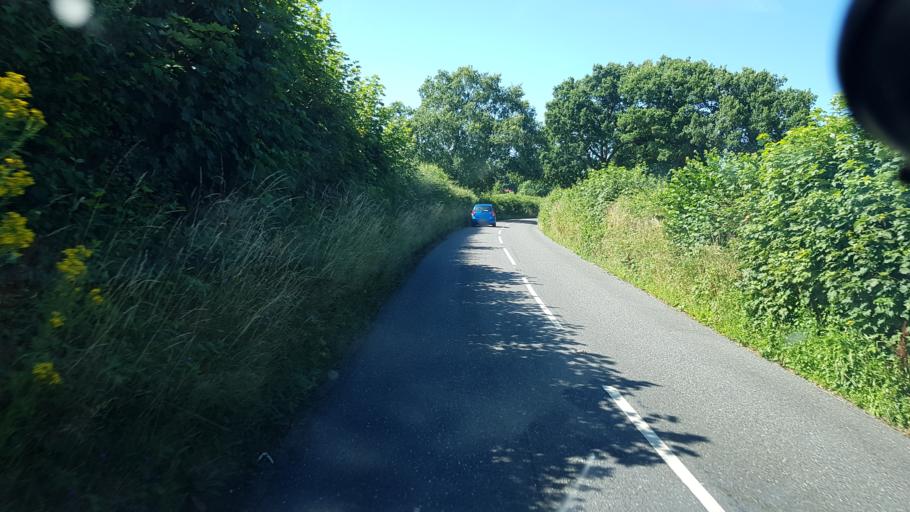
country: GB
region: England
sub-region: Kent
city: Westerham
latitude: 51.2313
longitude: 0.0685
